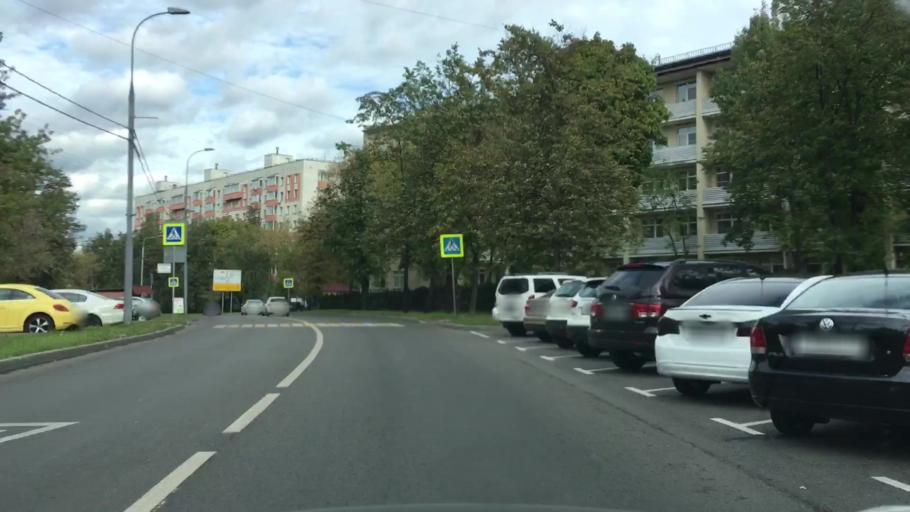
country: RU
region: Moscow
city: Gol'yanovo
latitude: 55.8009
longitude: 37.8288
